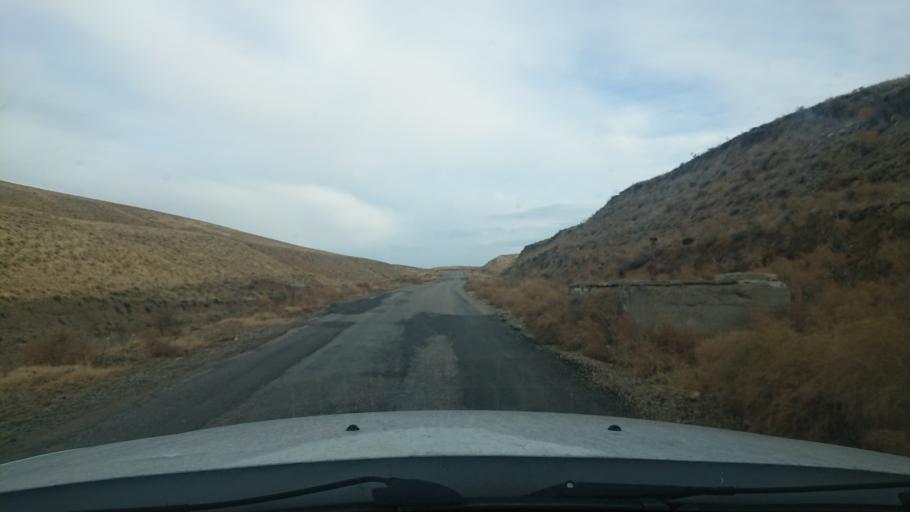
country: TR
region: Aksaray
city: Acipinar
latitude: 38.6303
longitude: 33.7998
